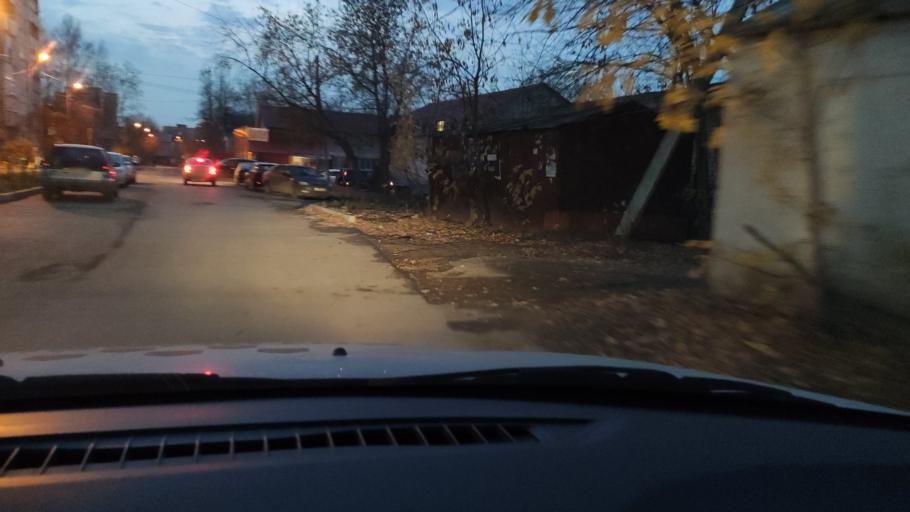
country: RU
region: Perm
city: Perm
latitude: 57.9894
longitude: 56.2147
